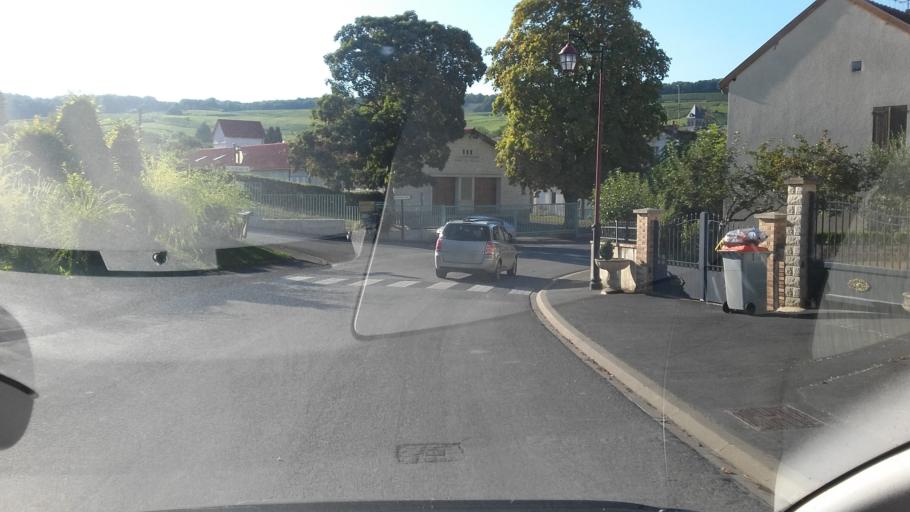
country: FR
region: Champagne-Ardenne
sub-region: Departement de la Marne
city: Le Mesnil-sur-Oger
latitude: 48.9576
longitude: 4.0152
